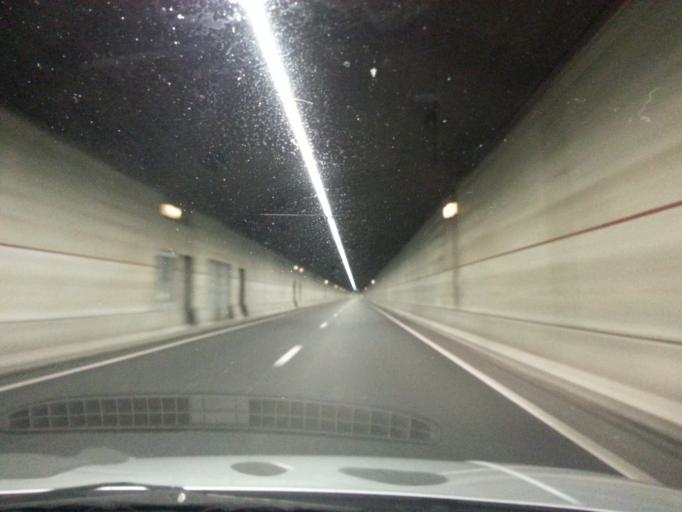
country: NL
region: North Holland
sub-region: Gemeente Diemen
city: Diemen
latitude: 52.3725
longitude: 4.9474
